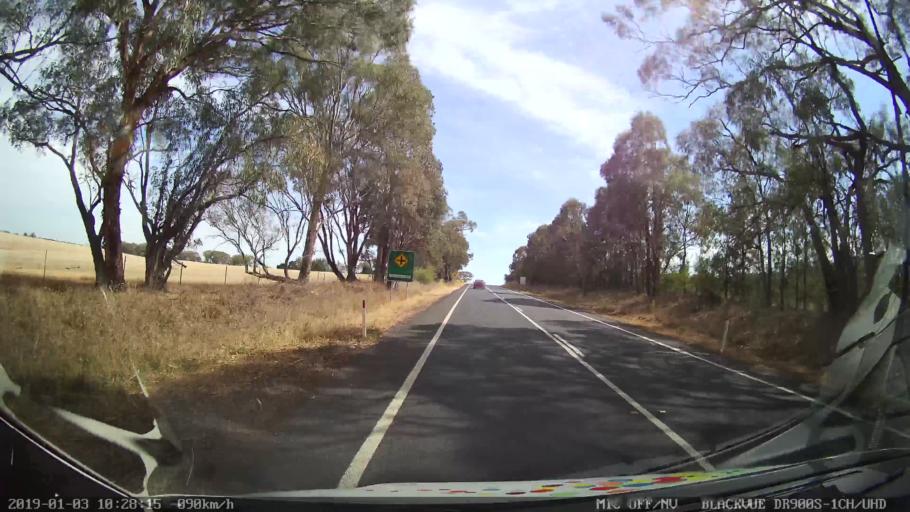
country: AU
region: New South Wales
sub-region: Young
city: Young
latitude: -34.3904
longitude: 148.2586
